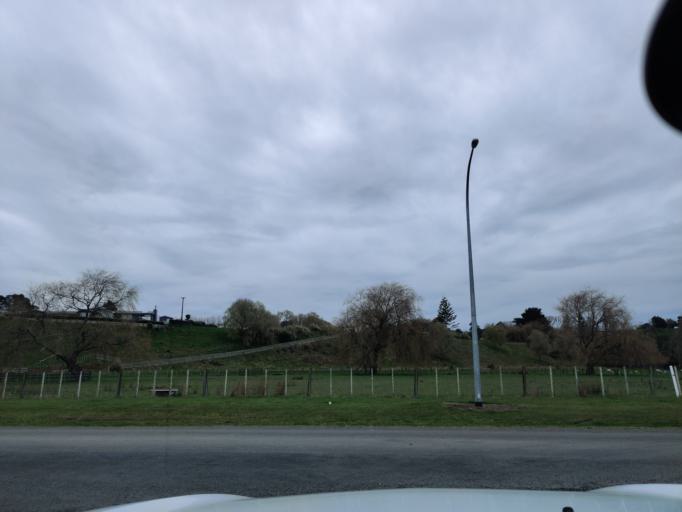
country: NZ
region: Manawatu-Wanganui
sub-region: Palmerston North City
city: Palmerston North
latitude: -40.2850
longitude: 175.7489
